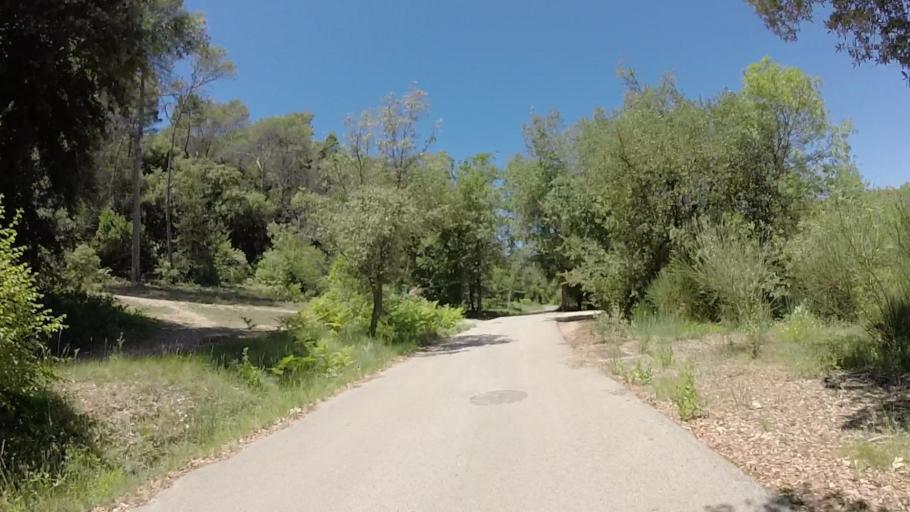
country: FR
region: Provence-Alpes-Cote d'Azur
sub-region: Departement des Alpes-Maritimes
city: Valbonne
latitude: 43.6304
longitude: 7.0261
